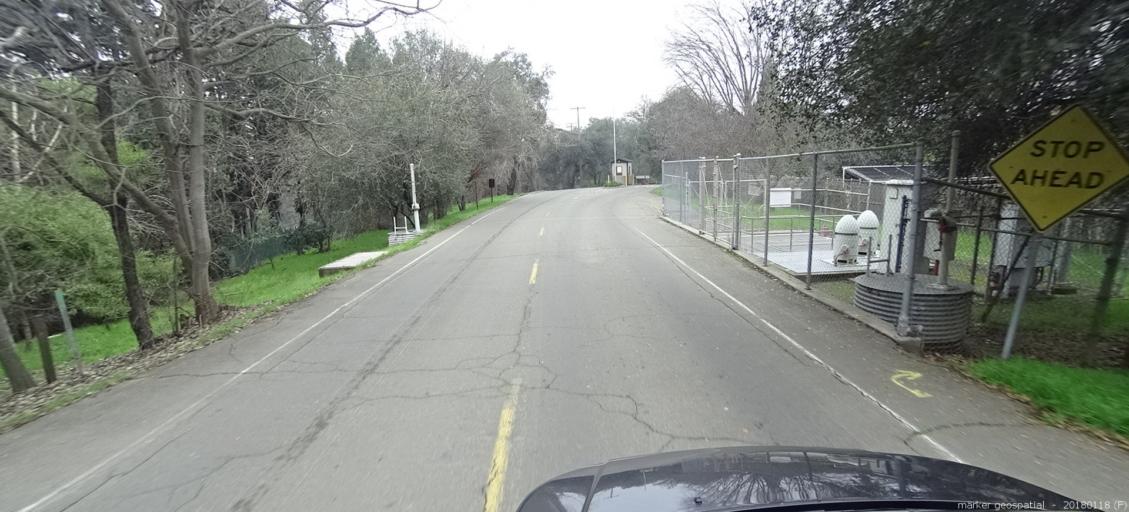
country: US
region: California
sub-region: Sacramento County
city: Rancho Cordova
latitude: 38.5881
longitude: -121.3243
